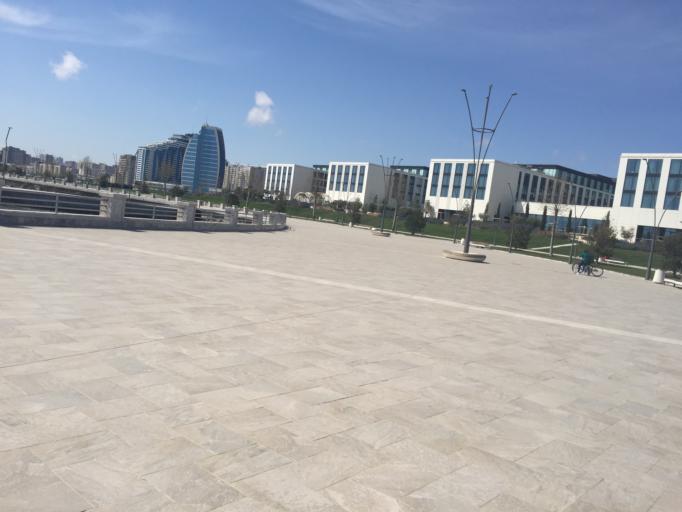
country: AZ
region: Baki
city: Baku
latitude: 40.3737
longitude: 49.8854
